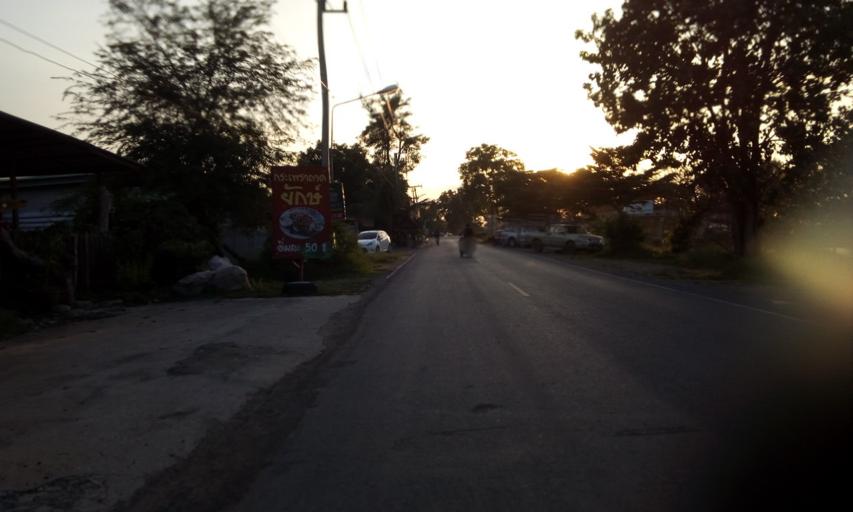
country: TH
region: Pathum Thani
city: Ban Rangsit
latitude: 14.0400
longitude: 100.7894
